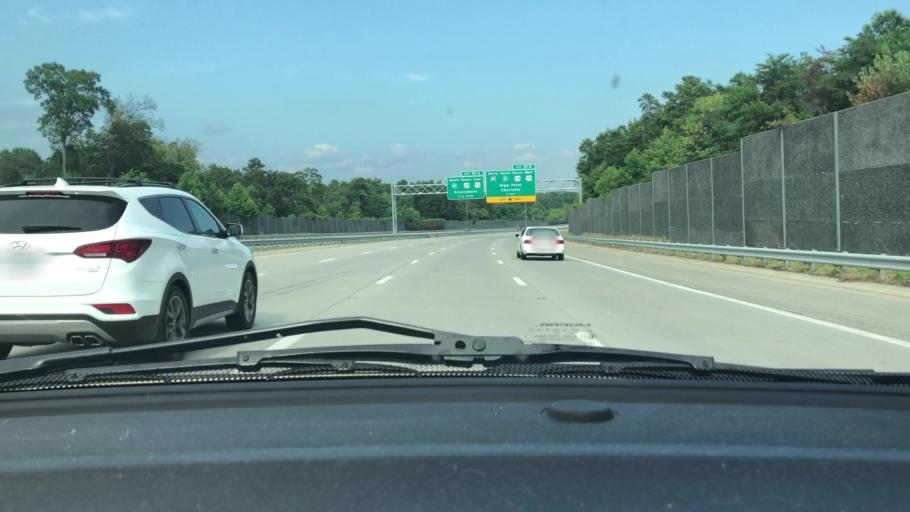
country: US
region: North Carolina
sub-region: Guilford County
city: Jamestown
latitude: 36.0210
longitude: -79.8635
